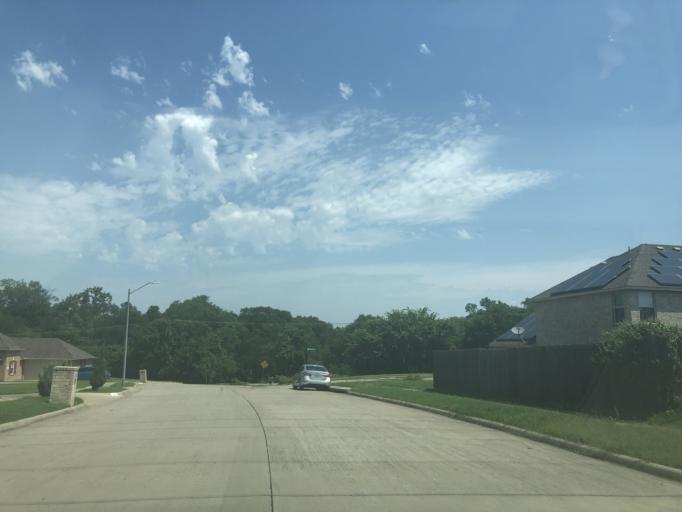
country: US
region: Texas
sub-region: Dallas County
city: Grand Prairie
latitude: 32.7278
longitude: -96.9999
